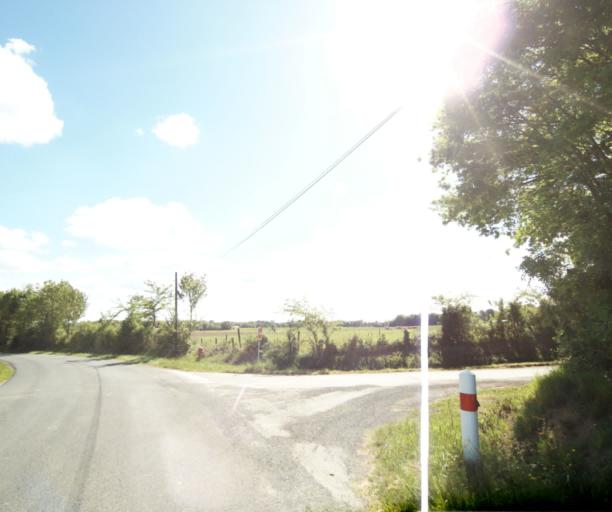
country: FR
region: Poitou-Charentes
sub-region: Departement de la Charente-Maritime
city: Saint-Georges-des-Coteaux
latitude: 45.7865
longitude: -0.6962
